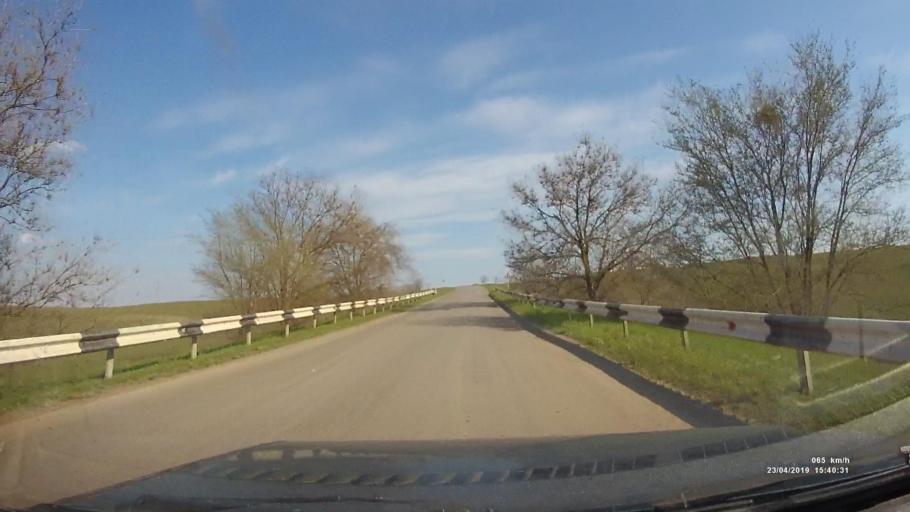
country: RU
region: Rostov
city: Remontnoye
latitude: 46.5551
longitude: 43.0390
